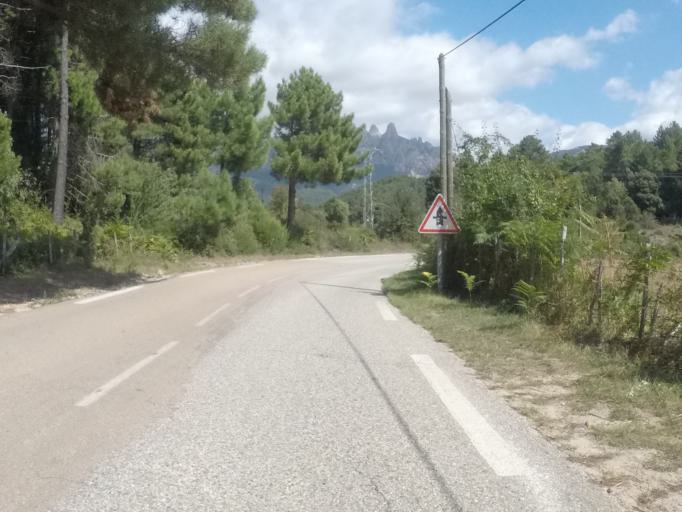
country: FR
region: Corsica
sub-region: Departement de la Corse-du-Sud
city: Zonza
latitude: 41.7591
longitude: 9.1834
